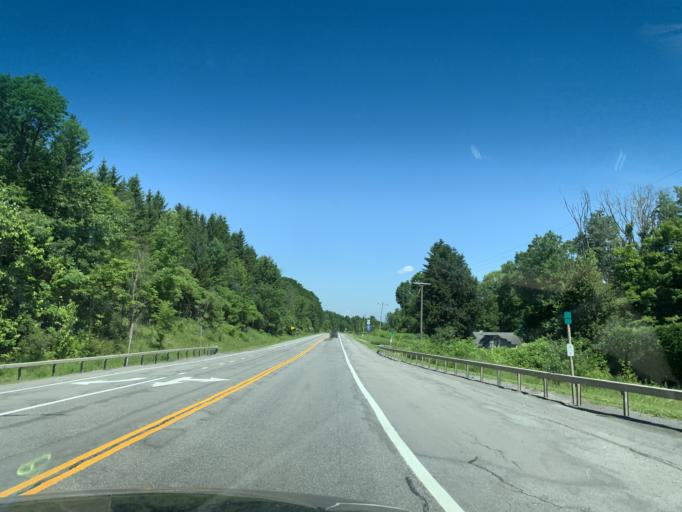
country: US
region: New York
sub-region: Oneida County
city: Chadwicks
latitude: 42.9802
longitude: -75.2530
